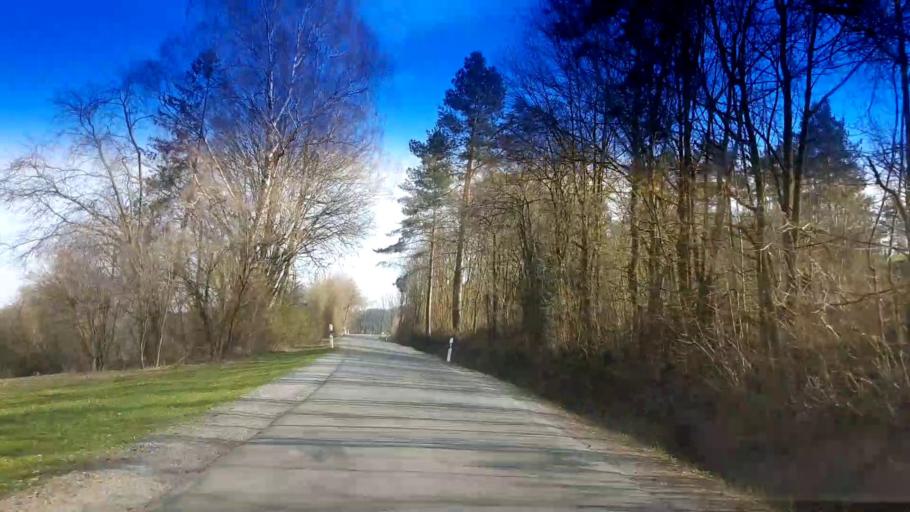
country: DE
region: Bavaria
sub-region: Upper Franconia
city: Neudrossenfeld
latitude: 50.0536
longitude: 11.5072
